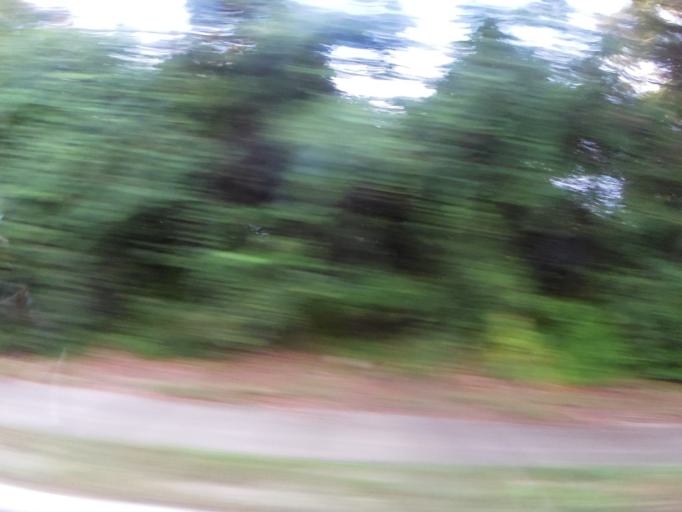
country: US
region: Florida
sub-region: Duval County
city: Atlantic Beach
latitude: 30.3744
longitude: -81.5030
